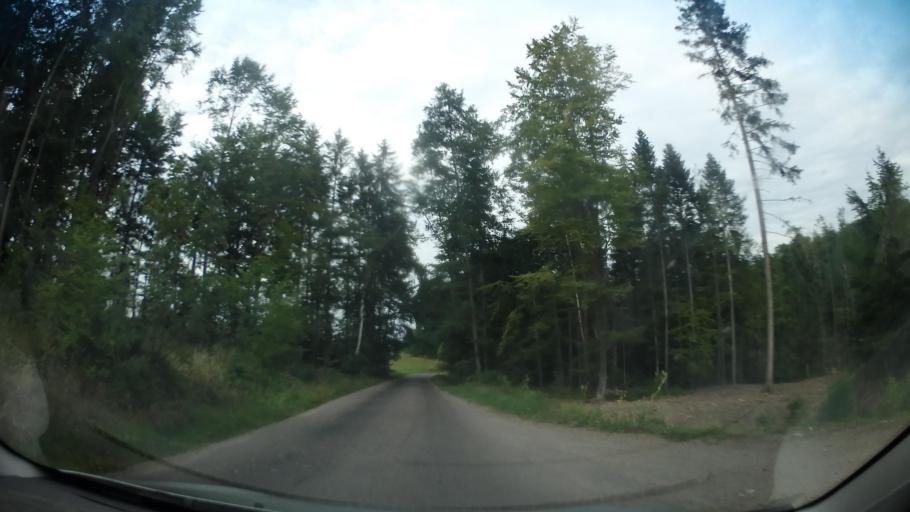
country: CZ
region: Pardubicky
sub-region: Okres Chrudim
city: Sec
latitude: 49.8264
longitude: 15.6965
